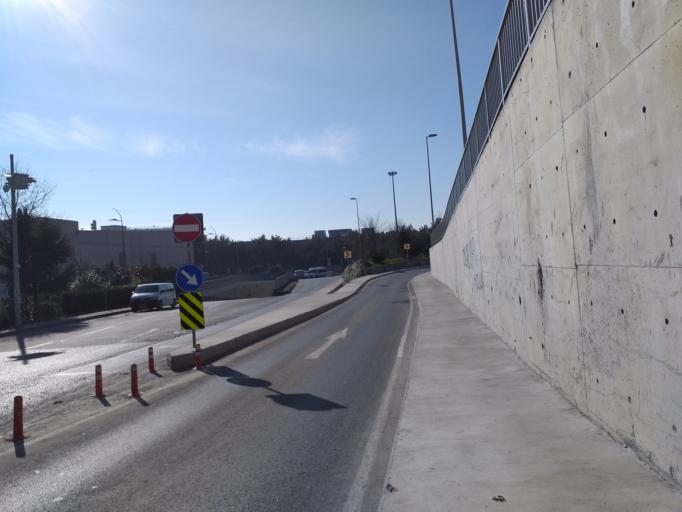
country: TR
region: Istanbul
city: Sisli
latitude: 41.1104
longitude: 29.0295
